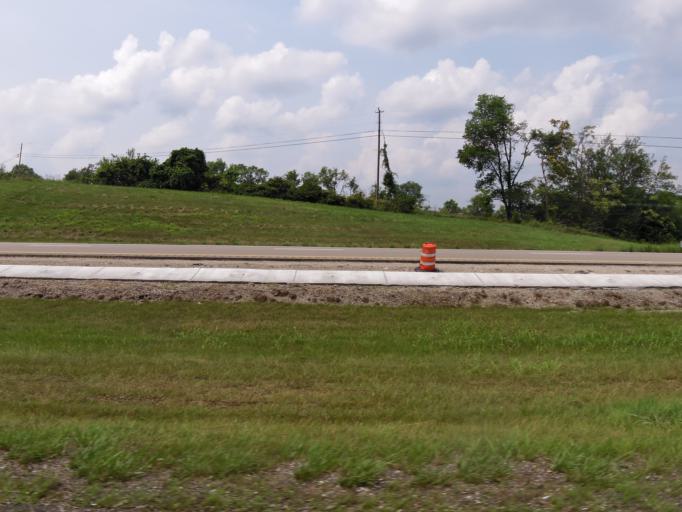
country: US
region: Indiana
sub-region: Switzerland County
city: Vevay
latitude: 38.6598
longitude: -85.0424
